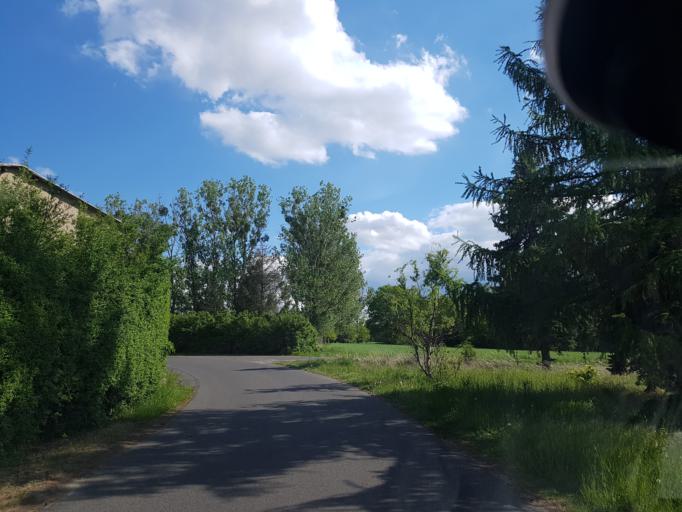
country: DE
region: Brandenburg
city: Drebkau
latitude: 51.6397
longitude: 14.2398
